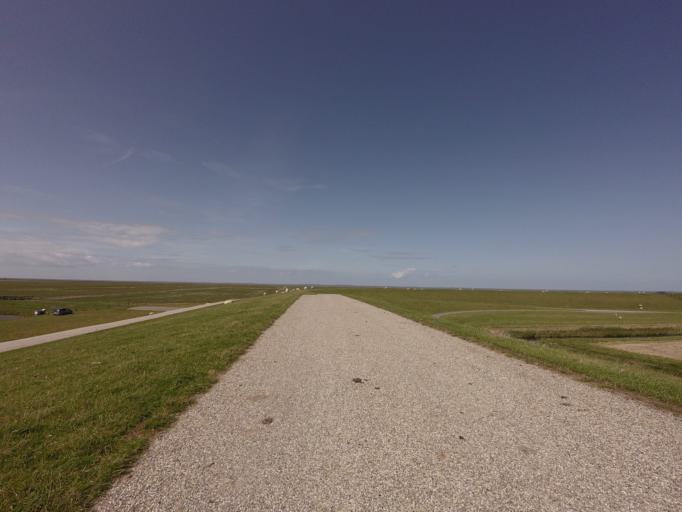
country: NL
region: Friesland
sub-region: Gemeente Dongeradeel
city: Holwerd
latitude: 53.3694
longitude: 5.8587
